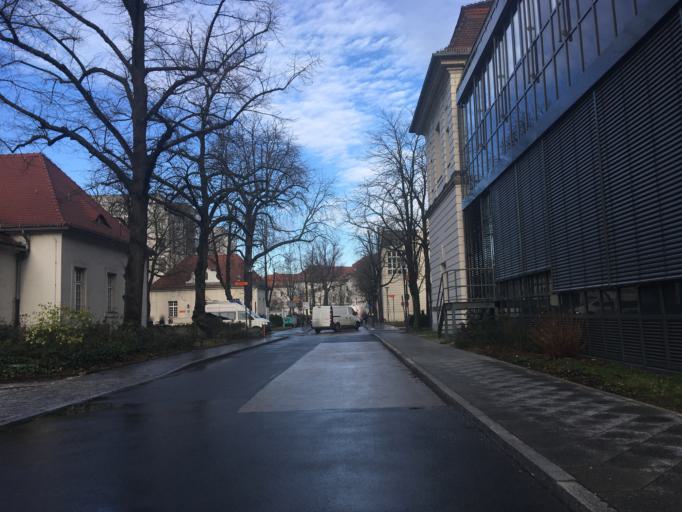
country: DE
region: Berlin
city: Wedding Bezirk
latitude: 52.5417
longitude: 13.3463
